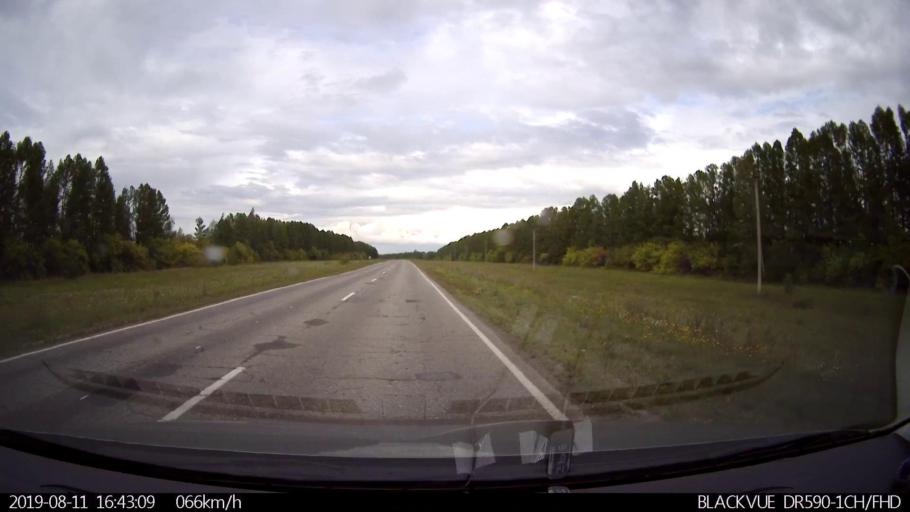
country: RU
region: Ulyanovsk
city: Mayna
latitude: 54.1664
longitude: 47.6691
